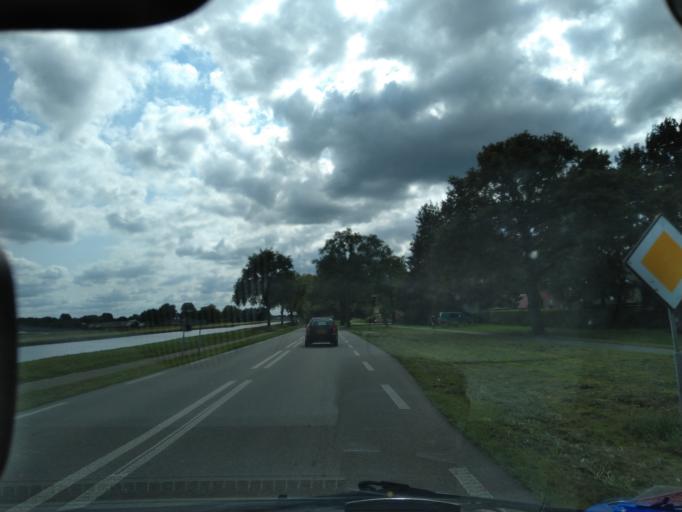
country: NL
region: Drenthe
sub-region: Gemeente Tynaarlo
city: Tynaarlo
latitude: 53.1101
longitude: 6.6043
